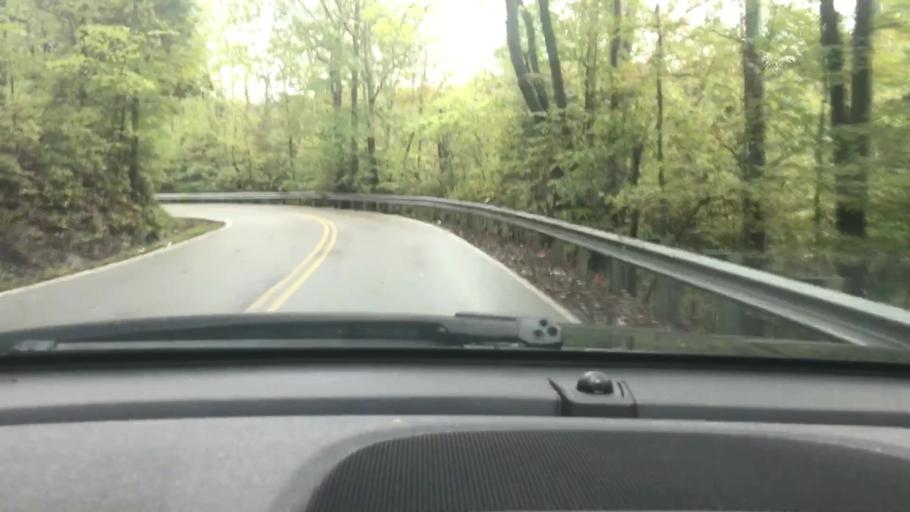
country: US
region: Tennessee
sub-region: Cheatham County
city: Kingston Springs
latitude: 36.1009
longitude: -87.1349
